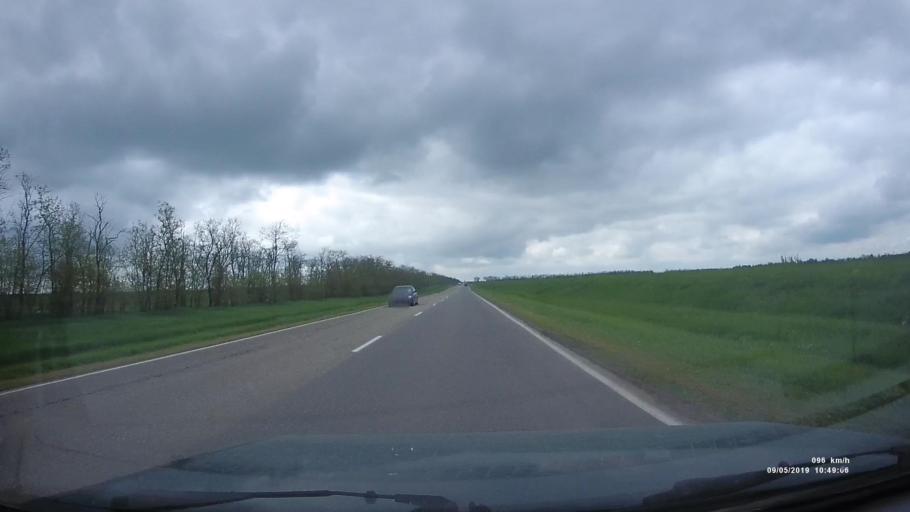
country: RU
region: Rostov
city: Peshkovo
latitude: 46.9473
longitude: 39.3562
